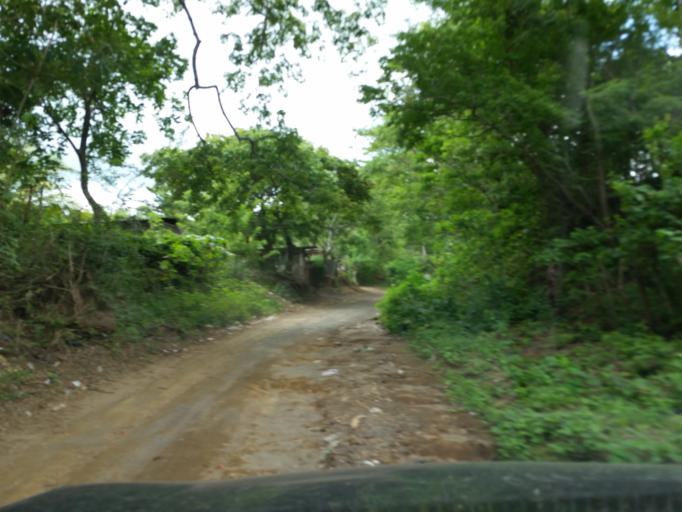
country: NI
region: Managua
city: Managua
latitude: 12.0843
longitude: -86.2731
